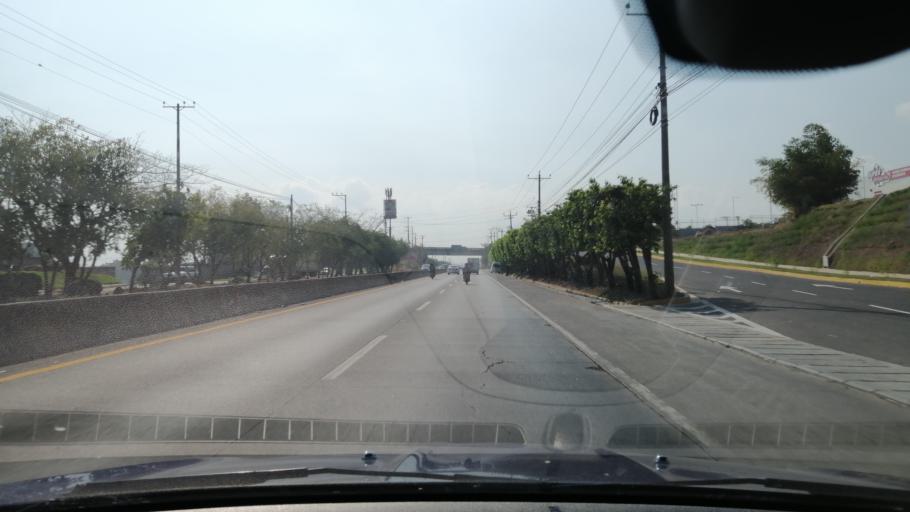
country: SV
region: San Salvador
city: Apopa
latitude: 13.7989
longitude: -89.2308
